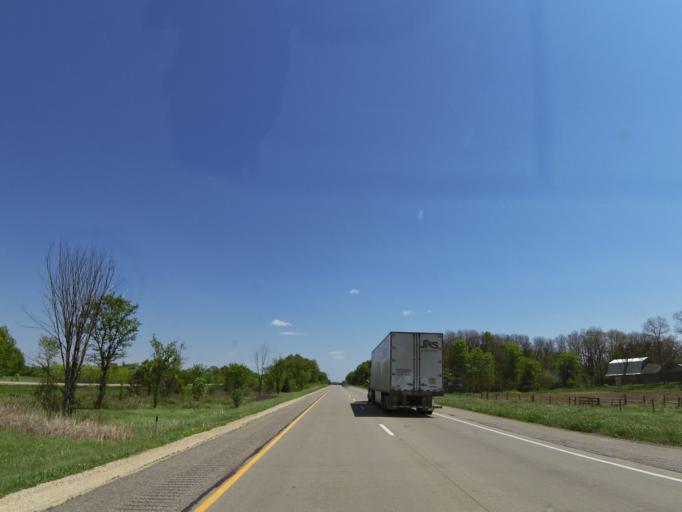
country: US
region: Wisconsin
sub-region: Juneau County
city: New Lisbon
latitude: 43.9003
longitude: -90.1933
